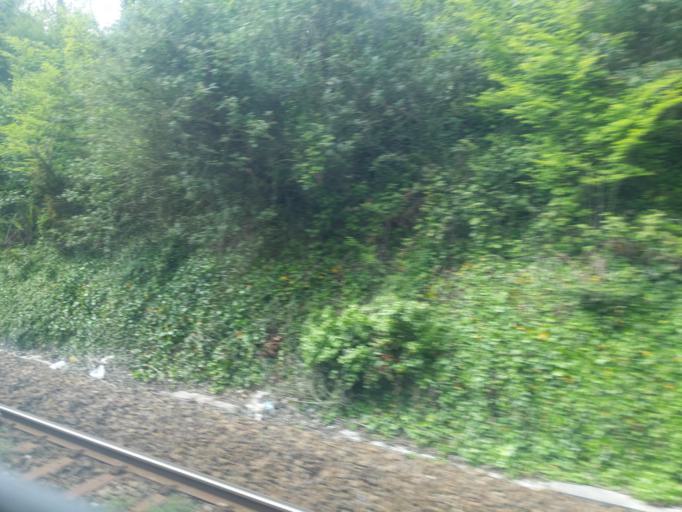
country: GB
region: England
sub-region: Cornwall
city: Camborne
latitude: 50.2092
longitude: -5.3006
